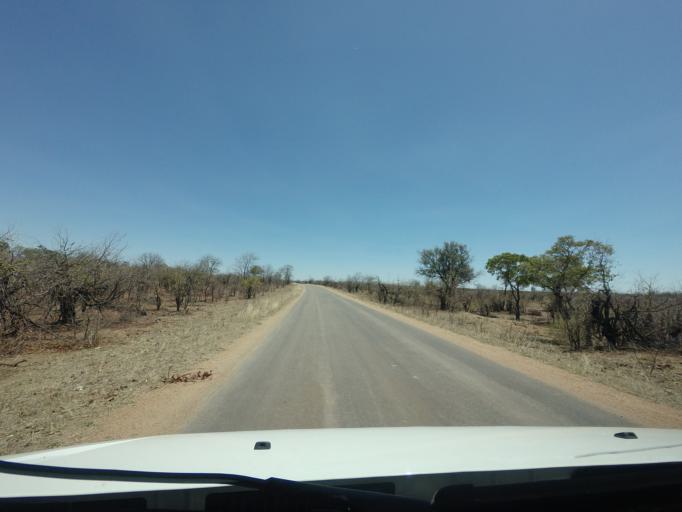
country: ZA
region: Limpopo
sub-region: Mopani District Municipality
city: Phalaborwa
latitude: -23.5547
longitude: 31.4456
